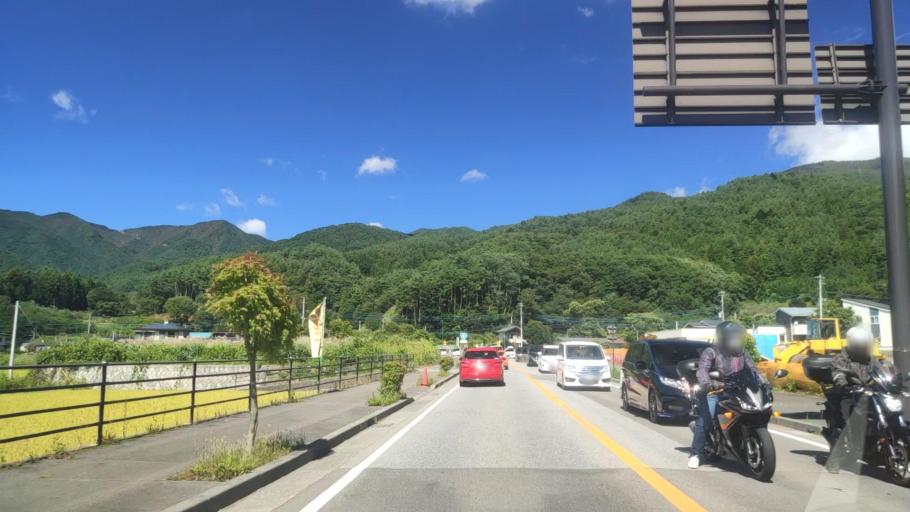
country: JP
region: Yamanashi
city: Fujikawaguchiko
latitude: 35.5228
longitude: 138.7776
